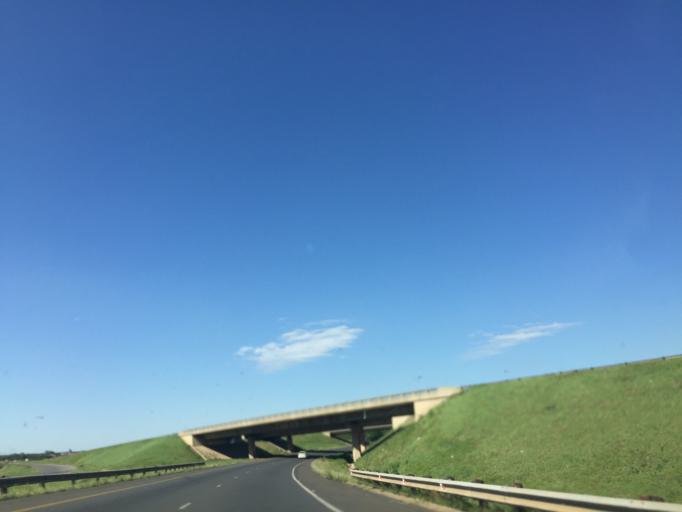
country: ZA
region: Gauteng
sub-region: Sedibeng District Municipality
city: Vereeniging
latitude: -26.6944
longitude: 27.9035
